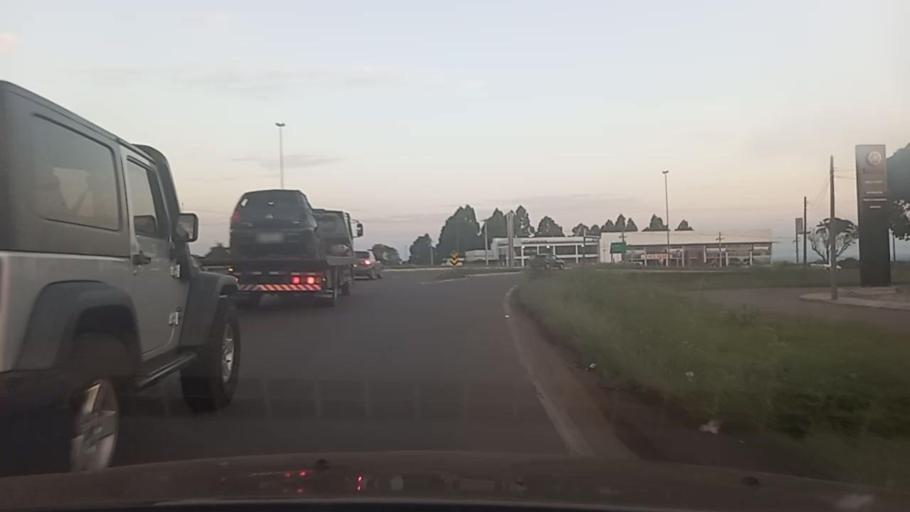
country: BR
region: Rio Grande do Sul
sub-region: Passo Fundo
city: Passo Fundo
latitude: -28.2699
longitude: -52.4413
